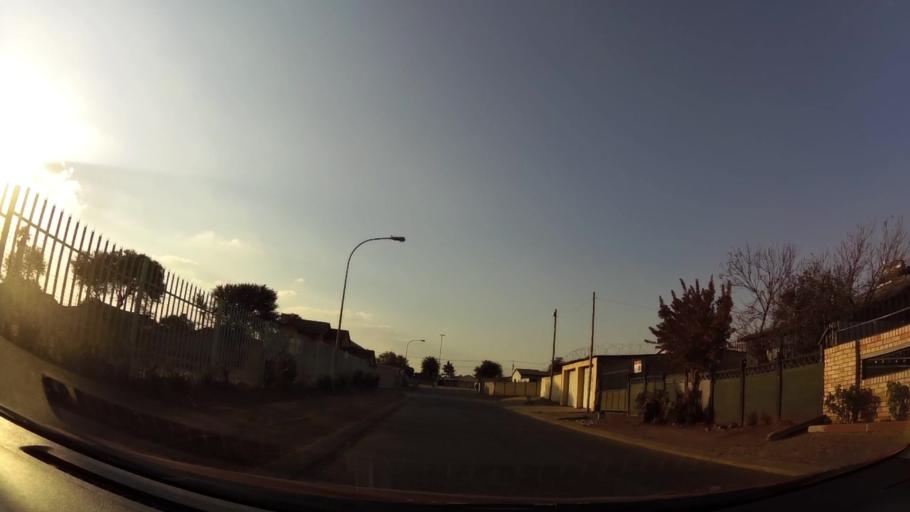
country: ZA
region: Gauteng
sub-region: City of Johannesburg Metropolitan Municipality
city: Soweto
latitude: -26.2816
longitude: 27.8952
